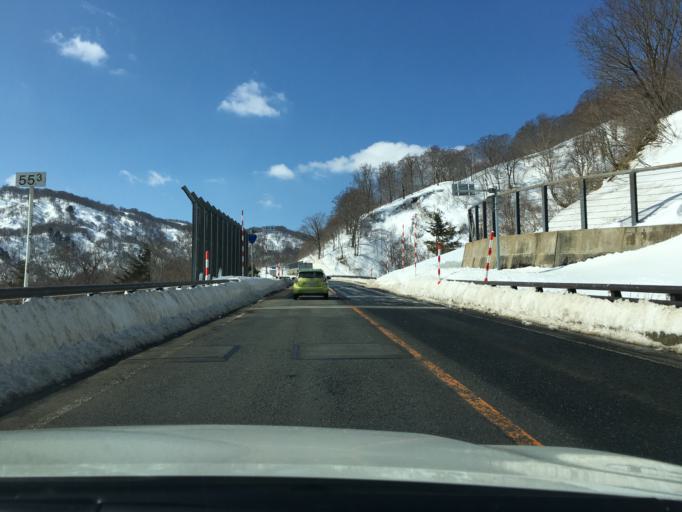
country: JP
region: Yamagata
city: Tsuruoka
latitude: 38.4924
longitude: 139.9808
